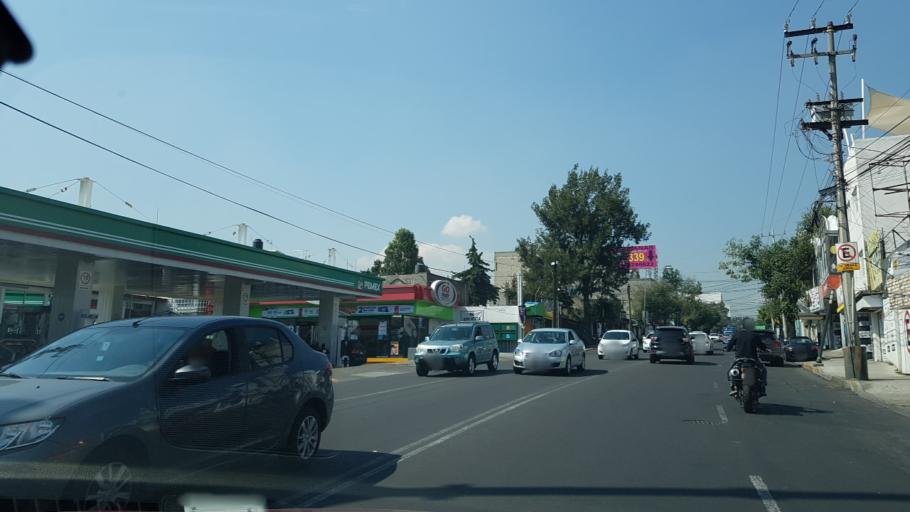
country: MX
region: Mexico City
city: Alvaro Obregon
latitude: 19.3513
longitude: -99.2184
